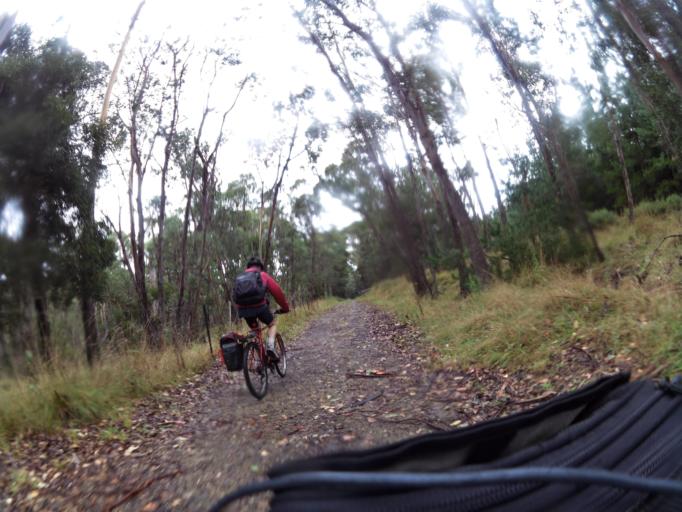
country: AU
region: New South Wales
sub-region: Greater Hume Shire
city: Holbrook
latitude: -36.1864
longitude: 147.5027
